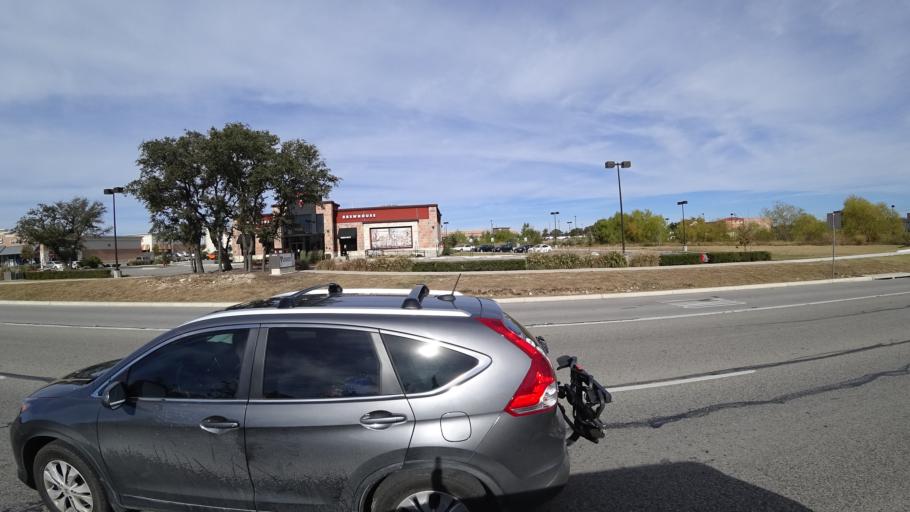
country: US
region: Texas
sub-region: Williamson County
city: Cedar Park
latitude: 30.5247
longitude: -97.8185
